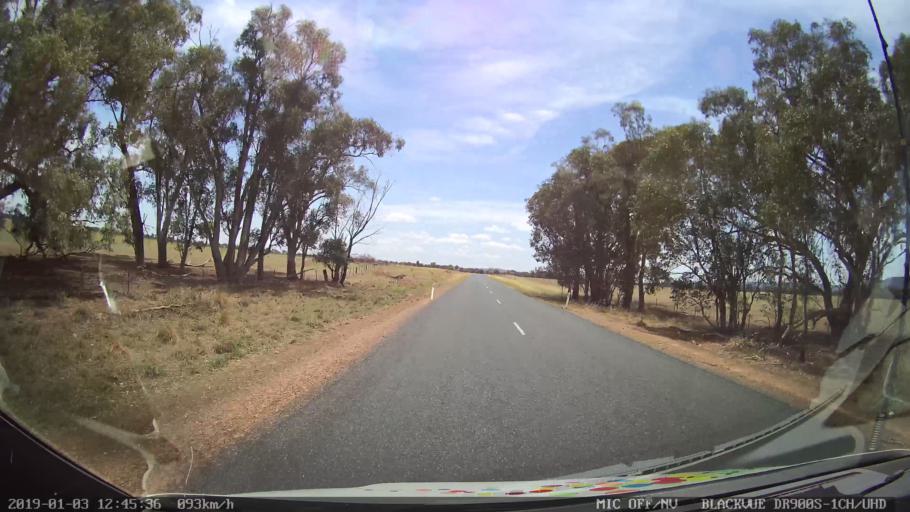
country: AU
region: New South Wales
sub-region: Weddin
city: Grenfell
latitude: -33.7477
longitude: 148.2248
